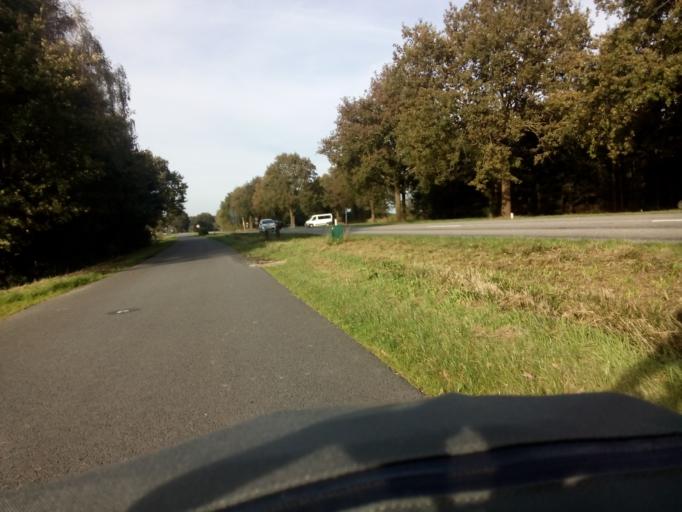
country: NL
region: Drenthe
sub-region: Gemeente Assen
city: Assen
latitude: 52.9409
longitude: 6.5472
